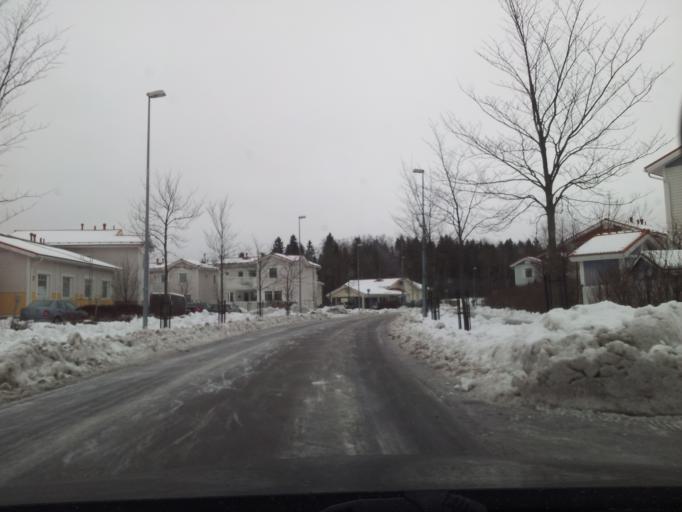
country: FI
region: Uusimaa
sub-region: Helsinki
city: Espoo
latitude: 60.1583
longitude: 24.5518
